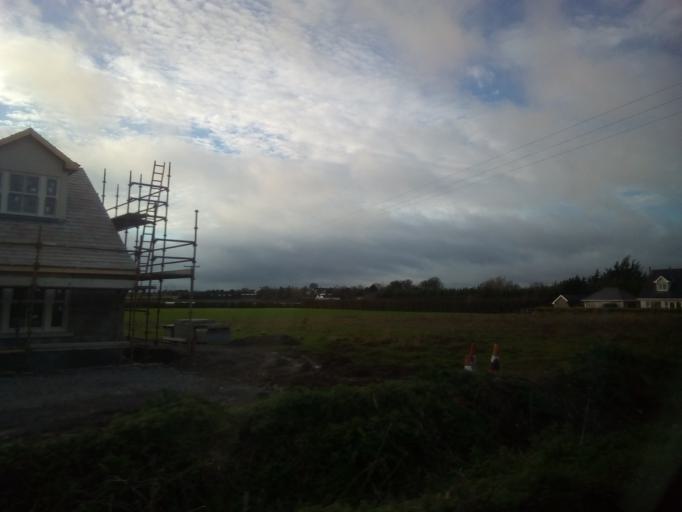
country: IE
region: Leinster
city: Balrothery
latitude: 53.5781
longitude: -6.1582
